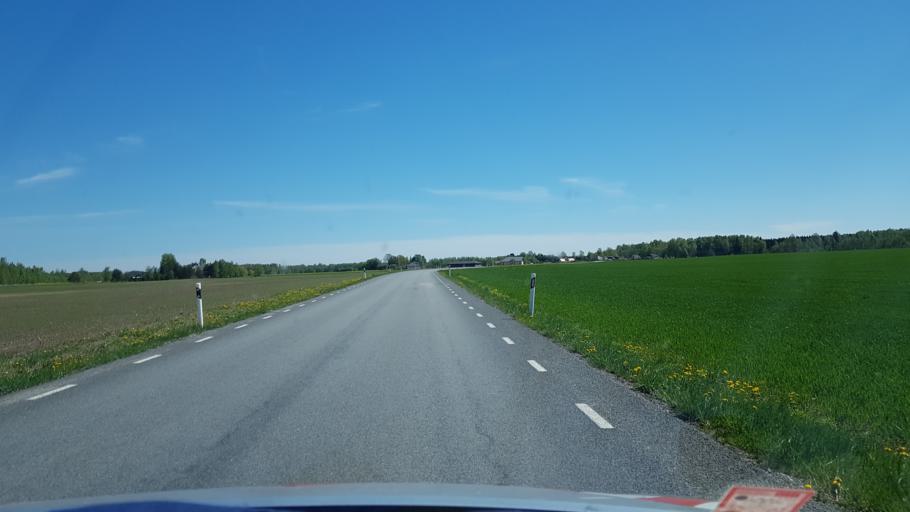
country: EE
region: Tartu
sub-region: UElenurme vald
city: Ulenurme
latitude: 58.3167
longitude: 26.6375
